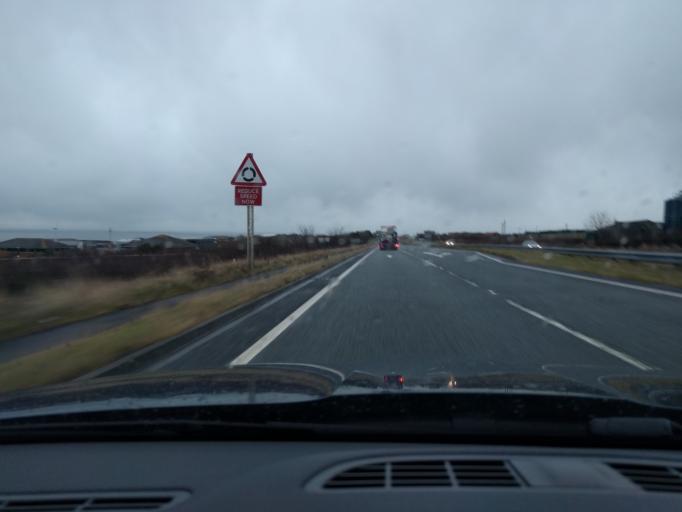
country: GB
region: England
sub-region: Northumberland
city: Berwick-Upon-Tweed
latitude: 55.7913
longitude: -2.0237
